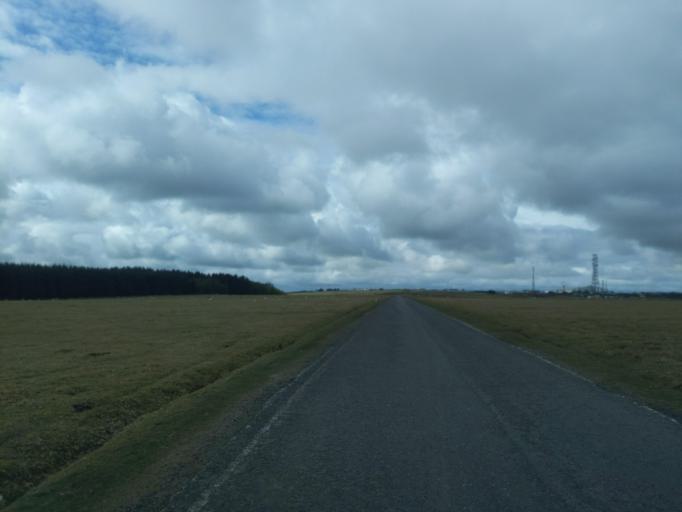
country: GB
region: England
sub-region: Cornwall
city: Camelford
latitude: 50.6363
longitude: -4.6200
